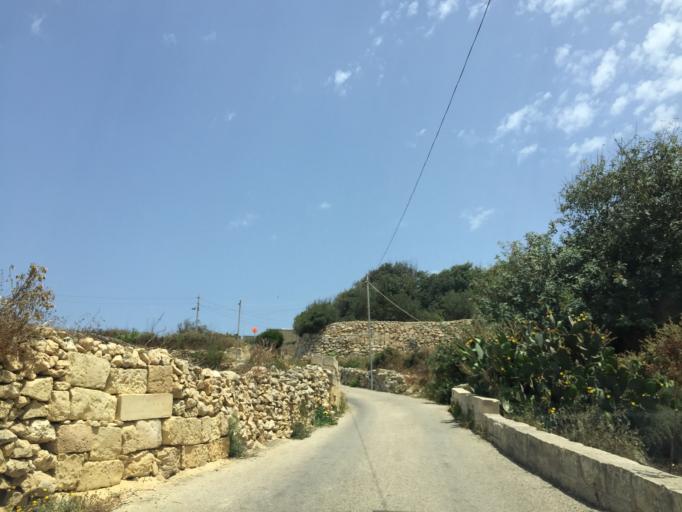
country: MT
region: Il-Fontana
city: Fontana
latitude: 36.0412
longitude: 14.2331
